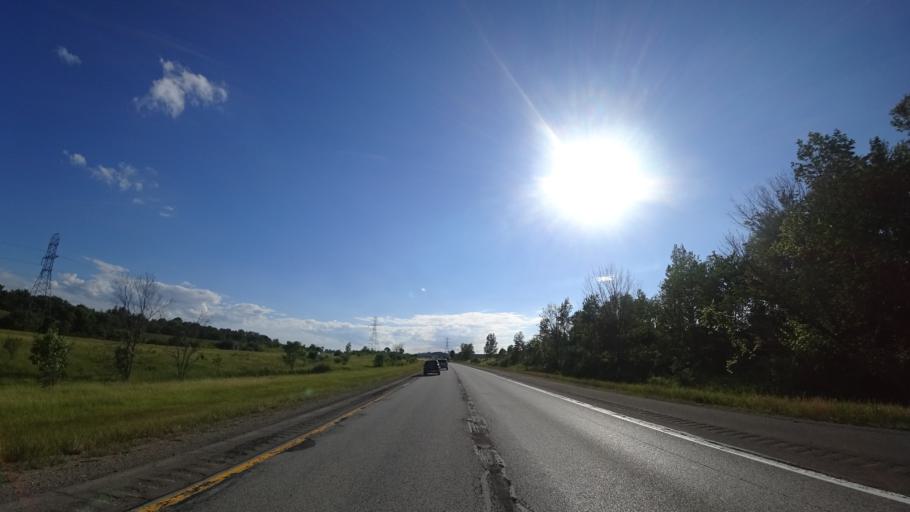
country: US
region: Michigan
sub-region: Ottawa County
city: Hudsonville
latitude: 42.8473
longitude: -85.8771
